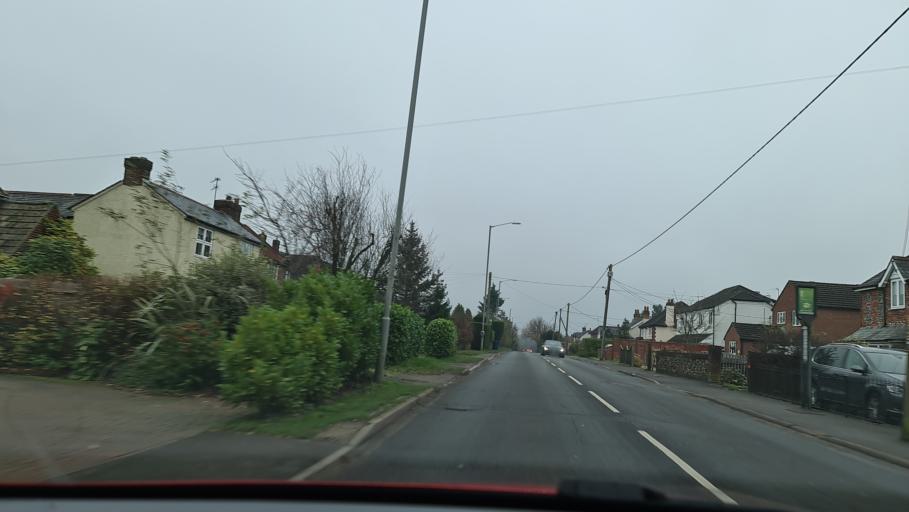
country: GB
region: England
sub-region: Buckinghamshire
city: High Wycombe
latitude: 51.6458
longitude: -0.6966
